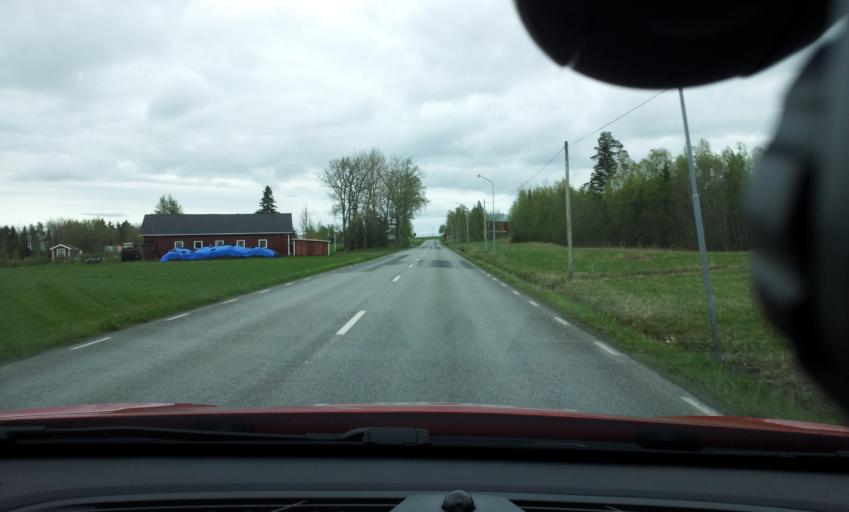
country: SE
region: Jaemtland
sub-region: OEstersunds Kommun
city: Ostersund
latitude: 63.1277
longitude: 14.6823
